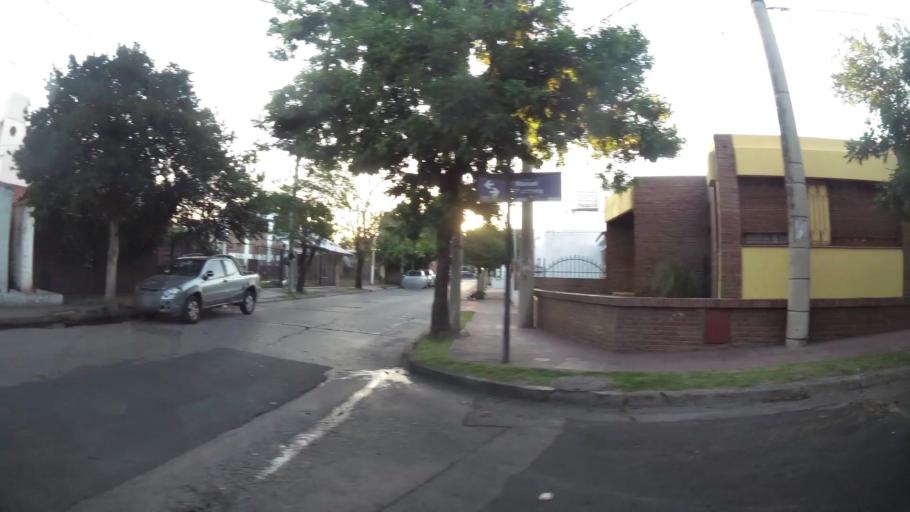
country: AR
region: Cordoba
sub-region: Departamento de Capital
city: Cordoba
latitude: -31.3830
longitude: -64.2212
